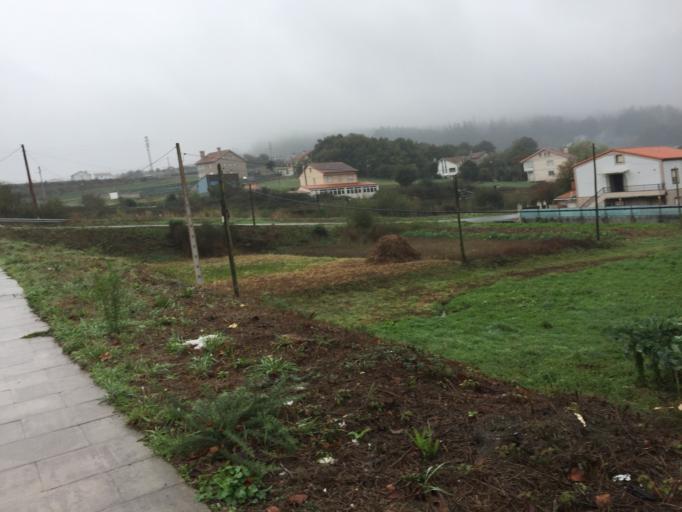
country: ES
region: Galicia
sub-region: Provincia da Coruna
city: Santiago de Compostela
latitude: 42.8556
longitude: -8.5397
